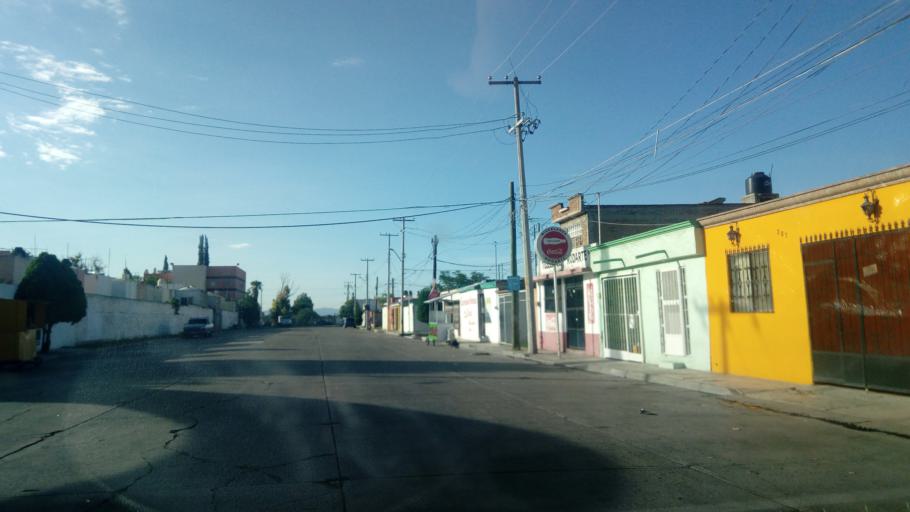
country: MX
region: Durango
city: Victoria de Durango
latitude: 24.0525
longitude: -104.6073
